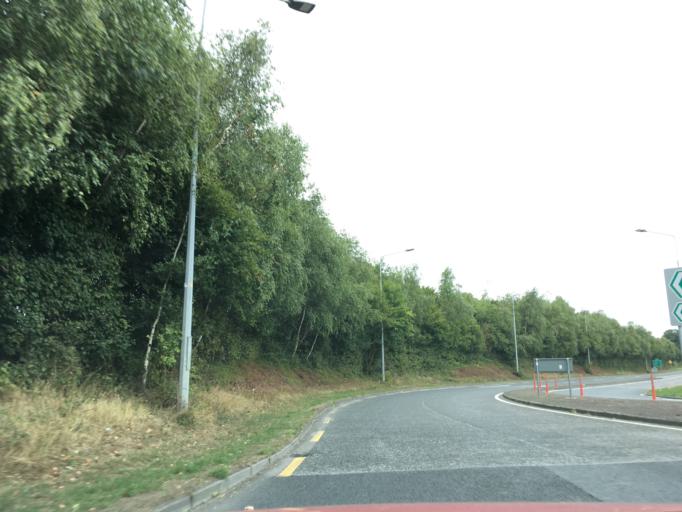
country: IE
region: Munster
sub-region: South Tipperary
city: Cluain Meala
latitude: 52.3678
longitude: -7.6136
